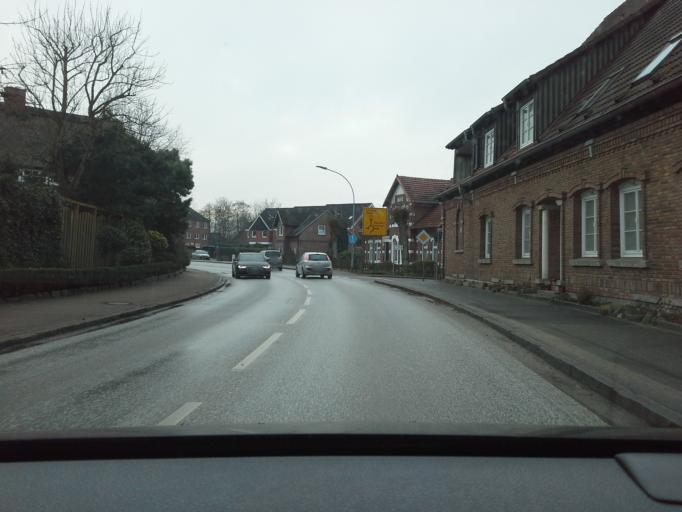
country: DE
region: Schleswig-Holstein
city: Holm
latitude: 53.6227
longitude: 9.6723
